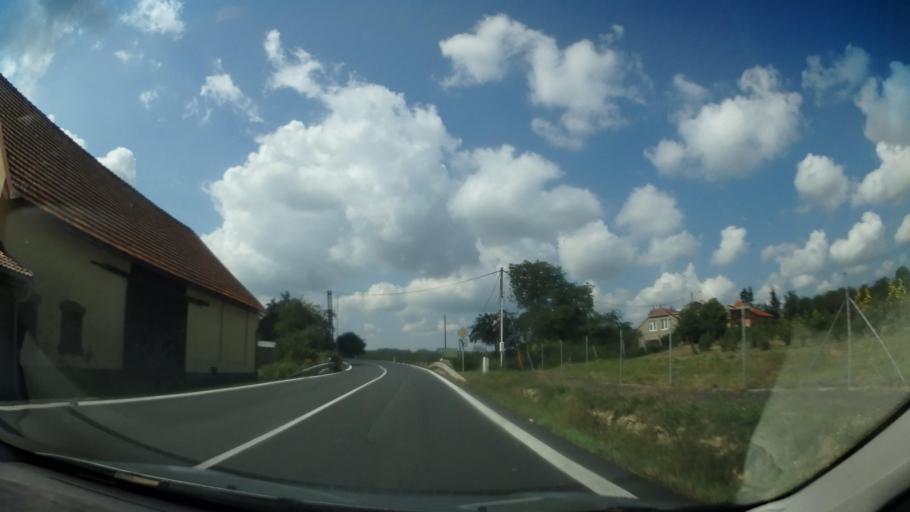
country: CZ
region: Central Bohemia
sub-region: Okres Kolin
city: Kourim
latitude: 49.9664
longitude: 14.9802
